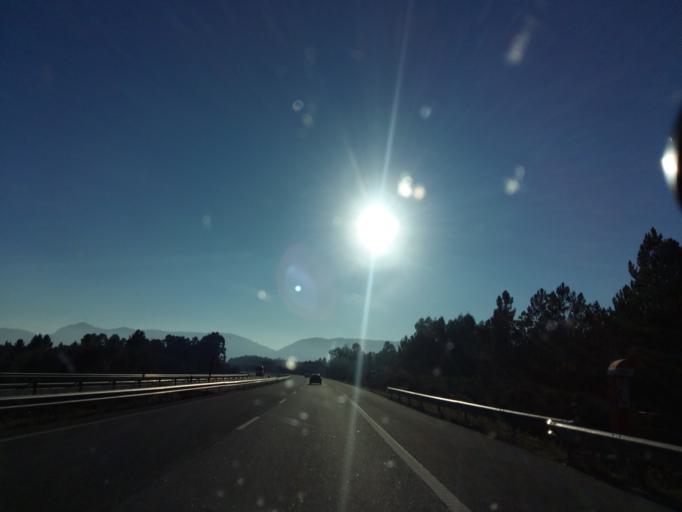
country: ES
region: Extremadura
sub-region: Provincia de Caceres
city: Cedillo
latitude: 39.7238
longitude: -7.6858
